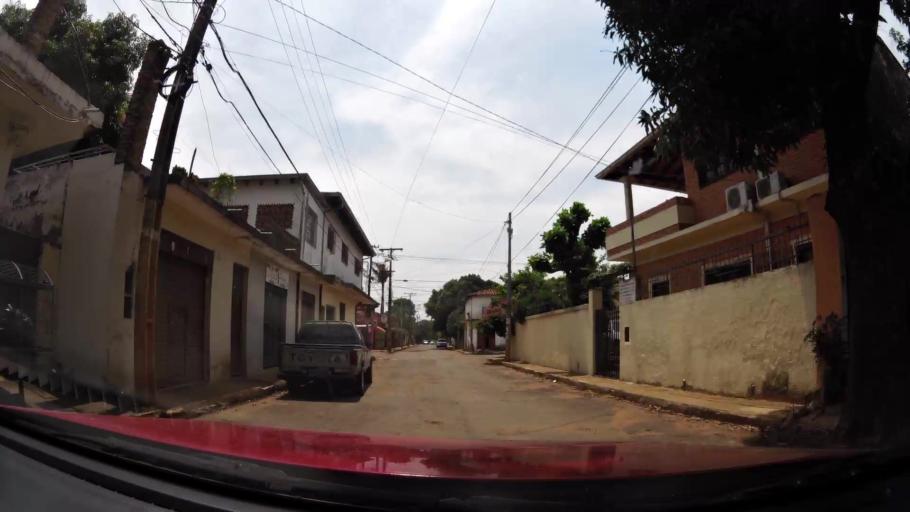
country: PY
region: Central
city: Fernando de la Mora
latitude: -25.3192
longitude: -57.5574
